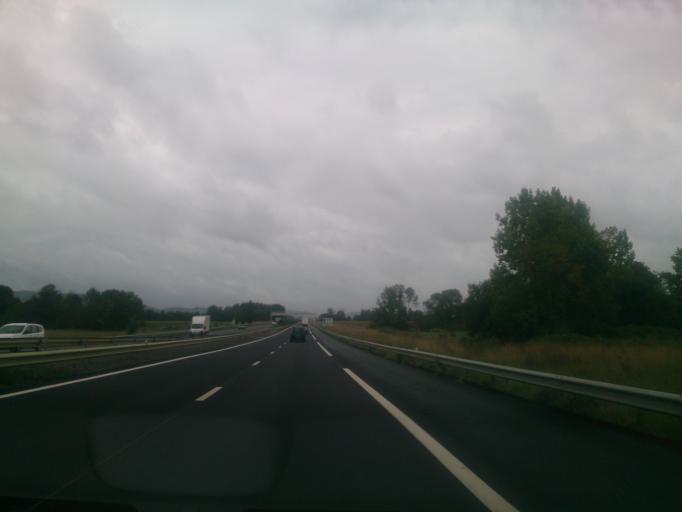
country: FR
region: Midi-Pyrenees
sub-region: Departement de la Haute-Garonne
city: Cazeres
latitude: 43.2249
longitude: 1.0544
